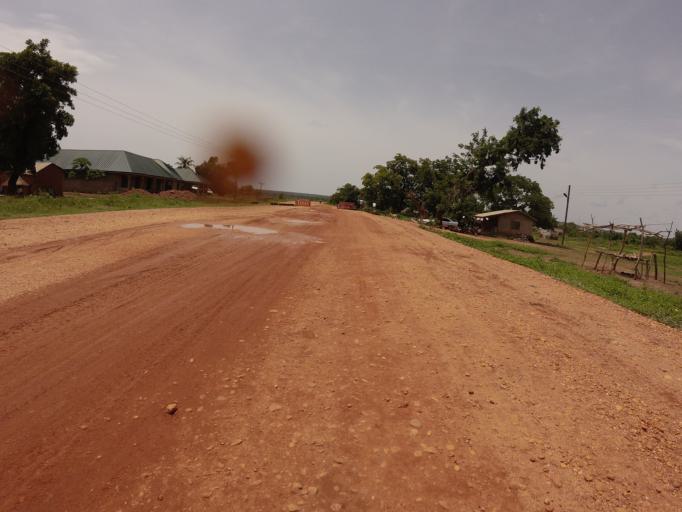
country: GH
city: Kpandae
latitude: 8.7049
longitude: 0.1623
